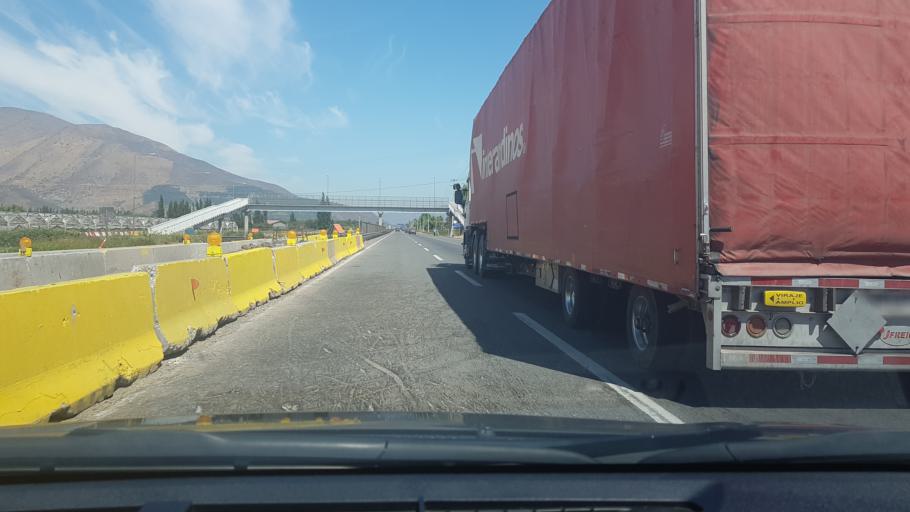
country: CL
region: Valparaiso
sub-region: Provincia de San Felipe
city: Llaillay
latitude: -32.8482
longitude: -70.9604
